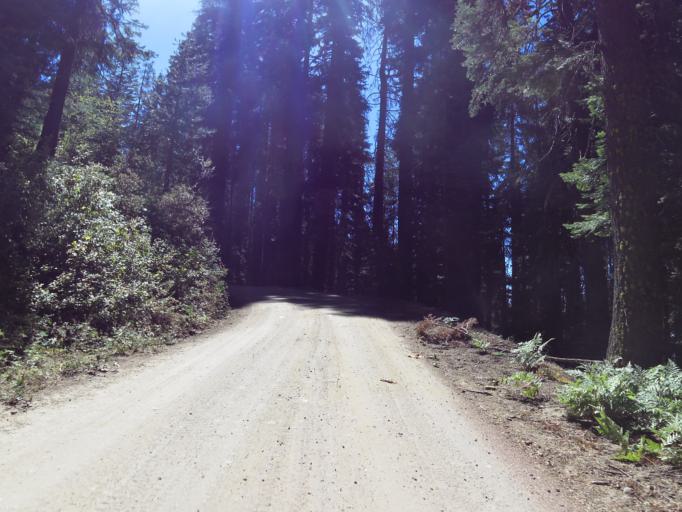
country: US
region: California
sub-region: Madera County
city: Oakhurst
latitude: 37.4452
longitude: -119.5199
